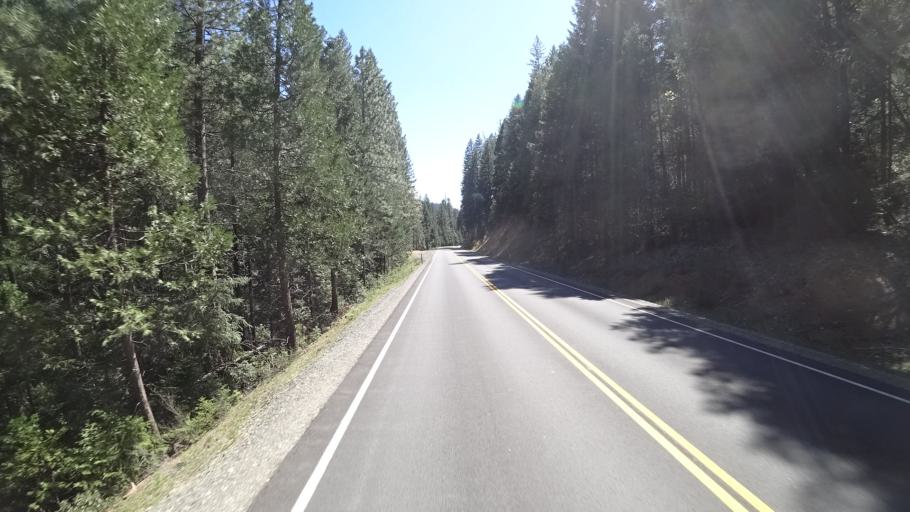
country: US
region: California
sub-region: Trinity County
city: Lewiston
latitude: 40.8995
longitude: -122.7866
